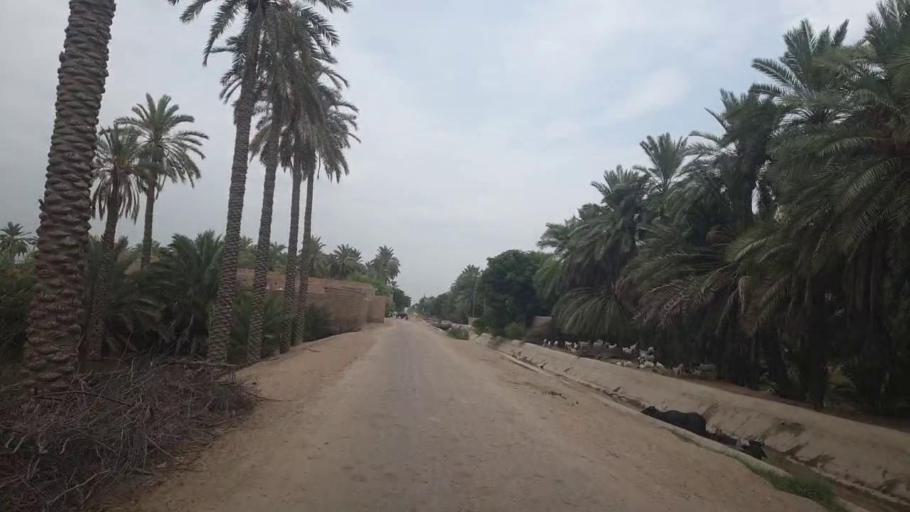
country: PK
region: Sindh
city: Khairpur
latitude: 27.5923
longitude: 68.7208
